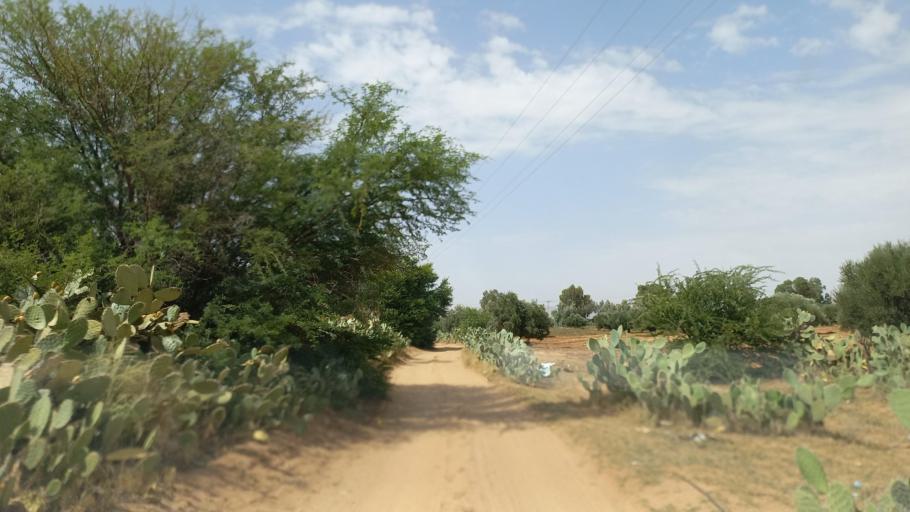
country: TN
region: Al Qasrayn
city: Kasserine
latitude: 35.2613
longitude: 9.0518
